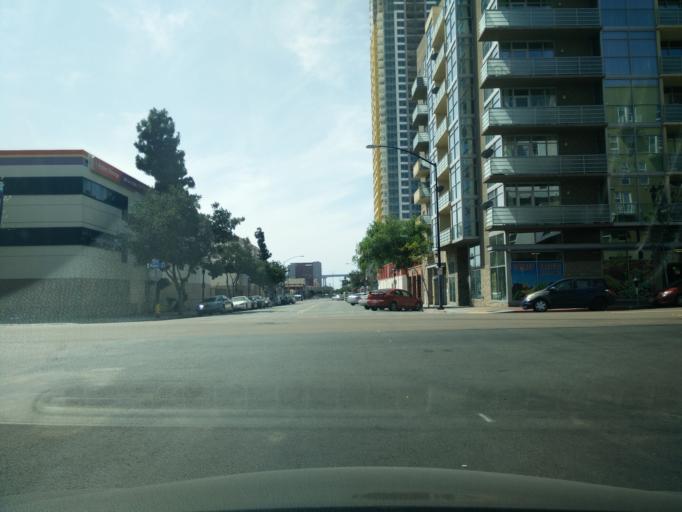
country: US
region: California
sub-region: San Diego County
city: San Diego
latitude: 32.7117
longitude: -117.1505
